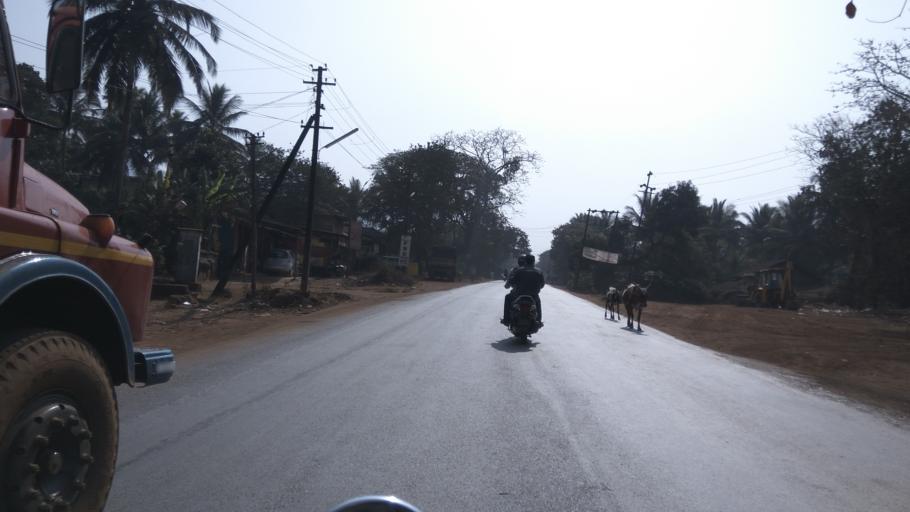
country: IN
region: Goa
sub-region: North Goa
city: Palle
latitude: 15.4125
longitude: 74.0848
